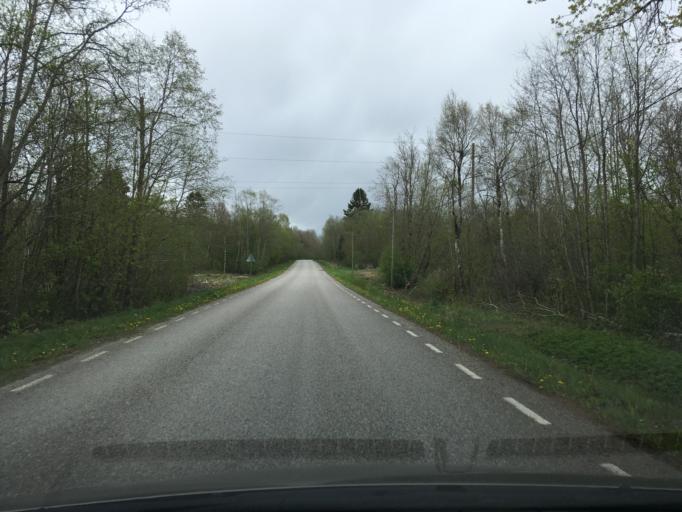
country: EE
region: Harju
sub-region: Rae vald
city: Vaida
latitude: 59.3515
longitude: 24.9961
